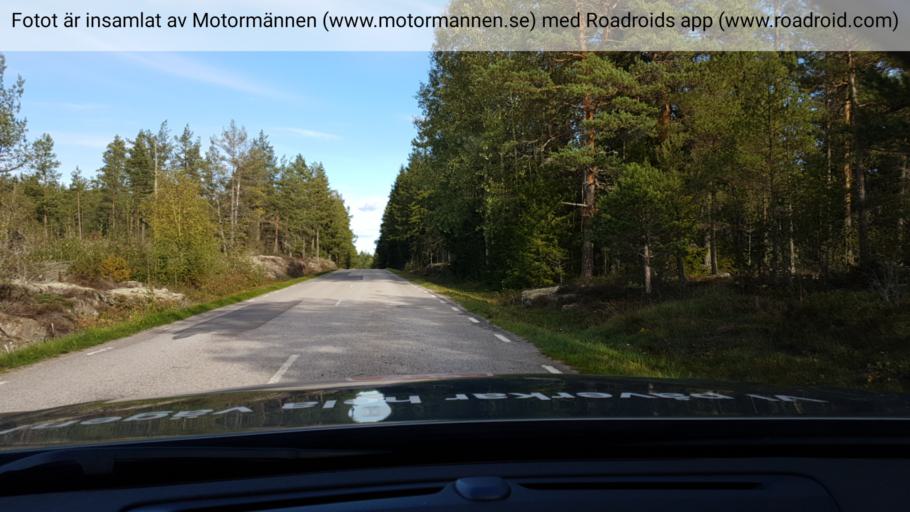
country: SE
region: Kalmar
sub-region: Vasterviks Kommun
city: Forserum
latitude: 58.0275
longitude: 16.5814
